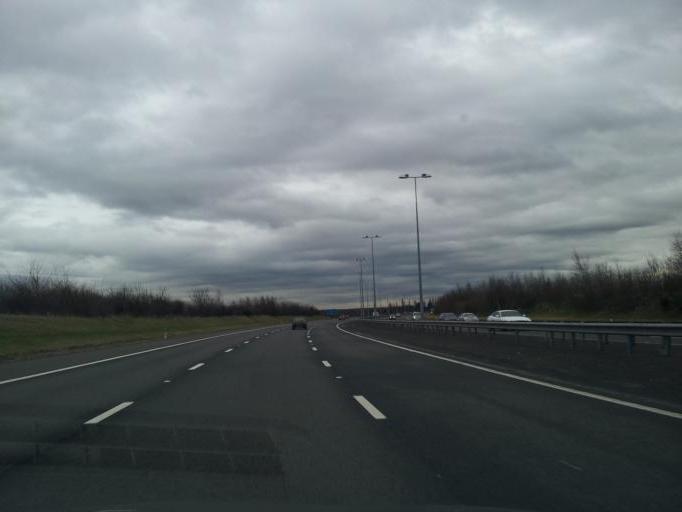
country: GB
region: England
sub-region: Warwickshire
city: Curdworth
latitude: 52.5485
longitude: -1.7317
